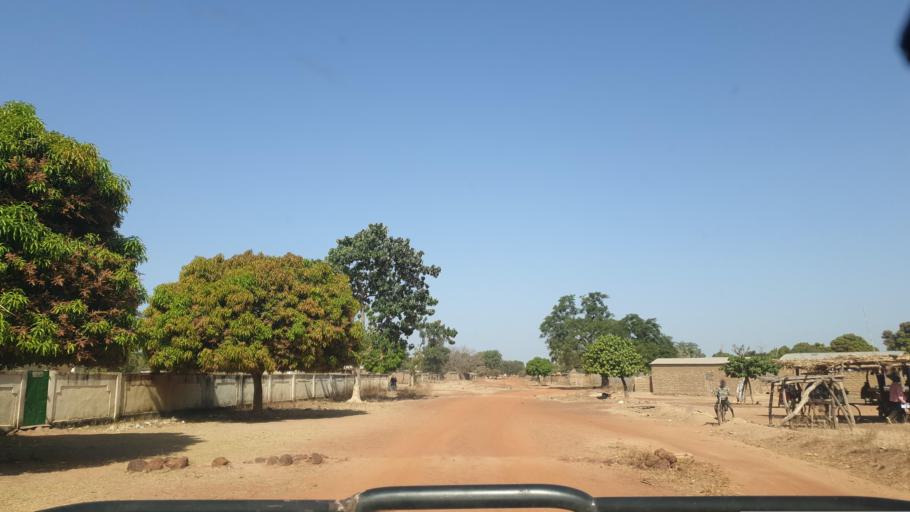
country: ML
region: Sikasso
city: Bougouni
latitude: 11.8130
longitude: -6.9351
